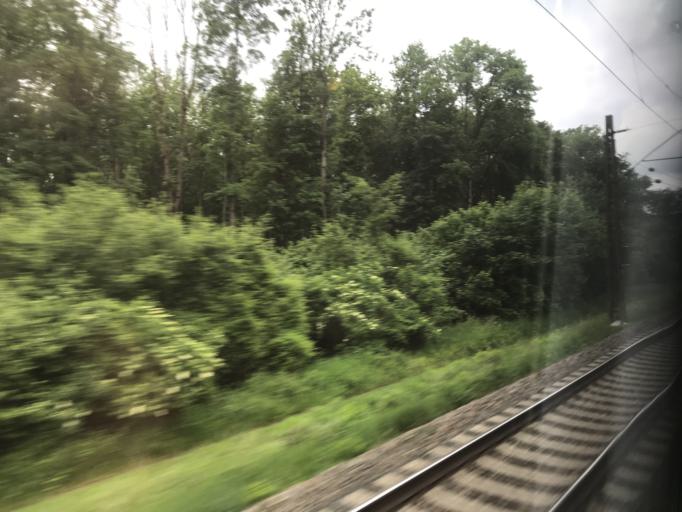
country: DE
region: Bavaria
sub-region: Swabia
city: Rettenbach
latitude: 48.4734
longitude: 10.3248
